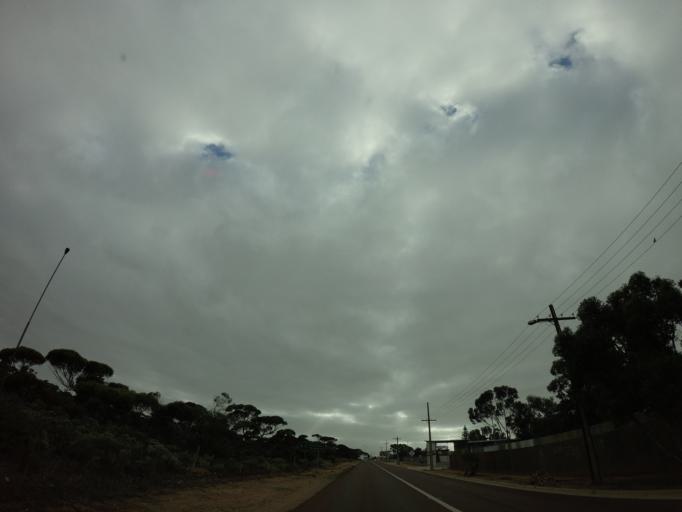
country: AU
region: South Australia
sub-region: Ceduna
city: Ceduna
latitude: -32.1220
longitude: 133.6811
